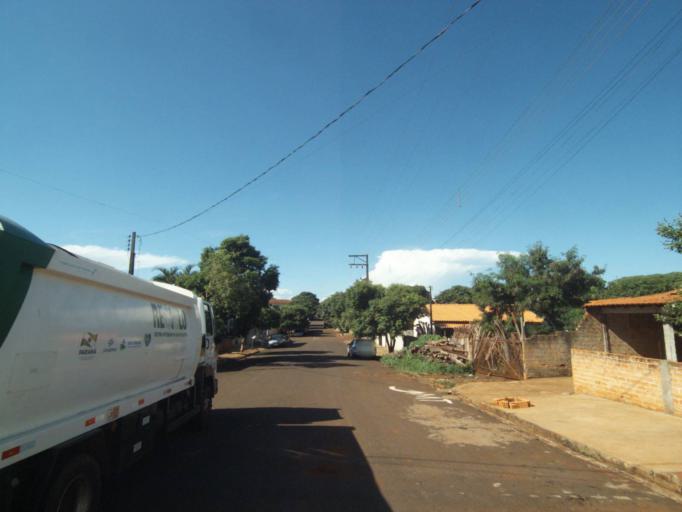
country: BR
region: Parana
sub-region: Sertanopolis
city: Sertanopolis
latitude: -23.0369
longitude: -50.8143
